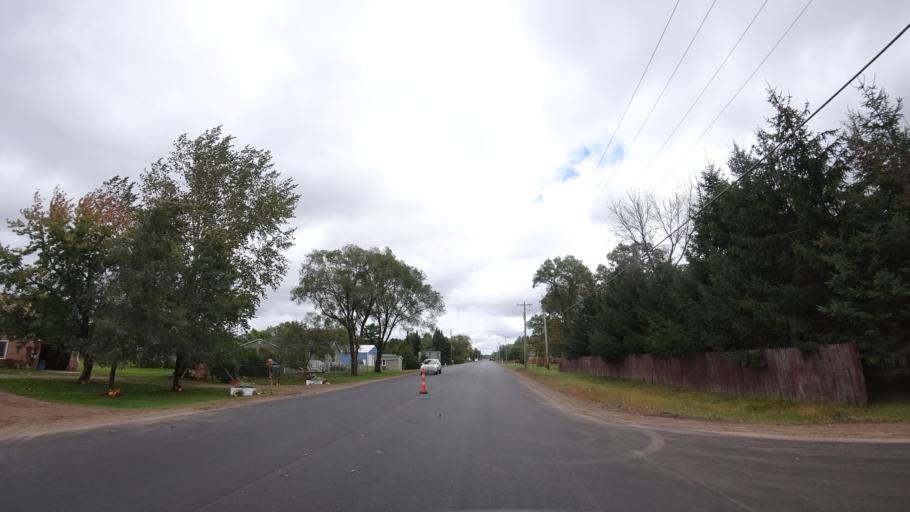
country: US
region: Wisconsin
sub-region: Chippewa County
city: Lake Wissota
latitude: 44.9295
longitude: -91.2780
